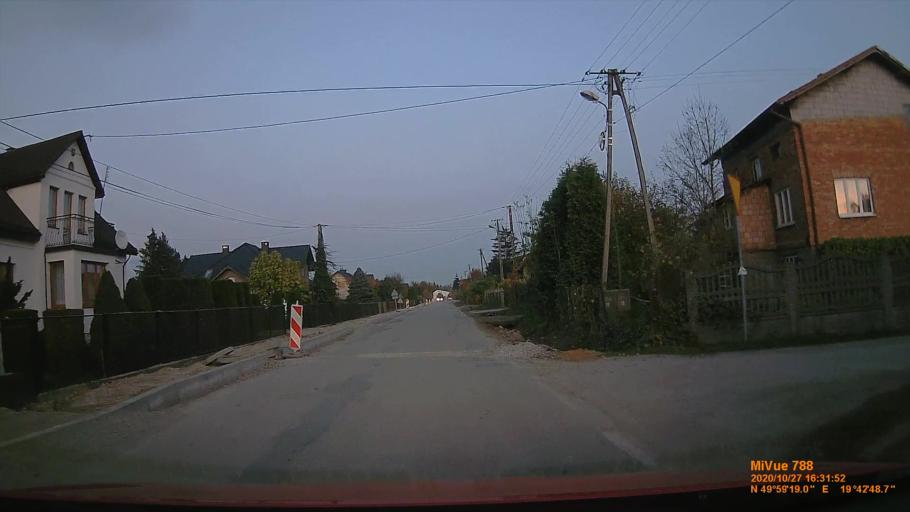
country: PL
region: Lesser Poland Voivodeship
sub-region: Powiat krakowski
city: Wolowice
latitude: 49.9886
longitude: 19.7137
